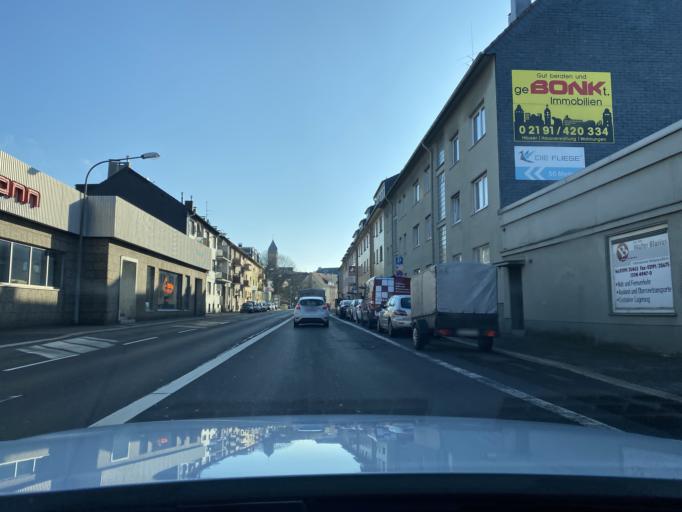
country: DE
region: North Rhine-Westphalia
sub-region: Regierungsbezirk Dusseldorf
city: Remscheid
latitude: 51.1774
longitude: 7.1887
